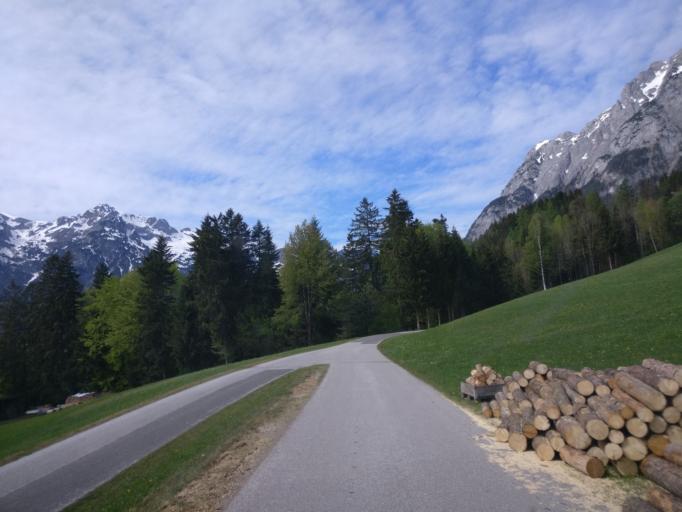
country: AT
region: Salzburg
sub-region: Politischer Bezirk Sankt Johann im Pongau
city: Pfarrwerfen
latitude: 47.4711
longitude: 13.2041
